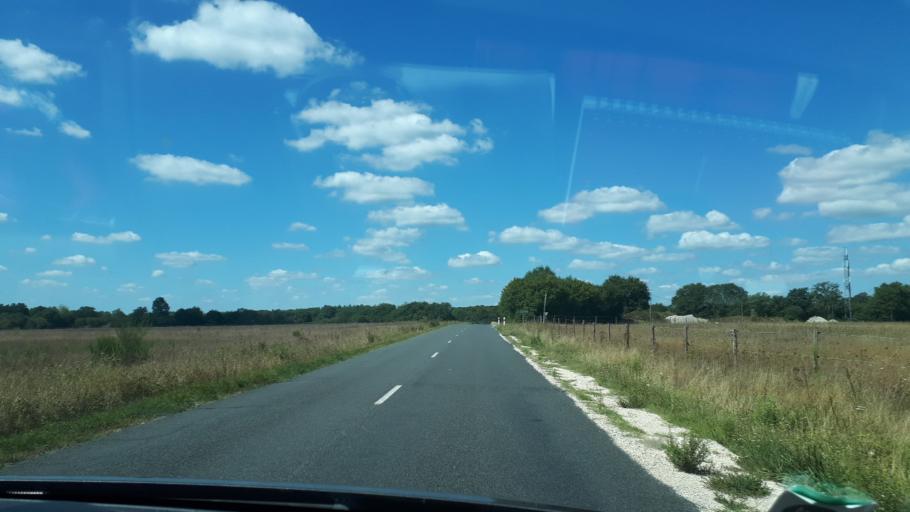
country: FR
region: Centre
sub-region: Departement du Loir-et-Cher
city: Neung-sur-Beuvron
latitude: 47.5351
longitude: 1.7870
